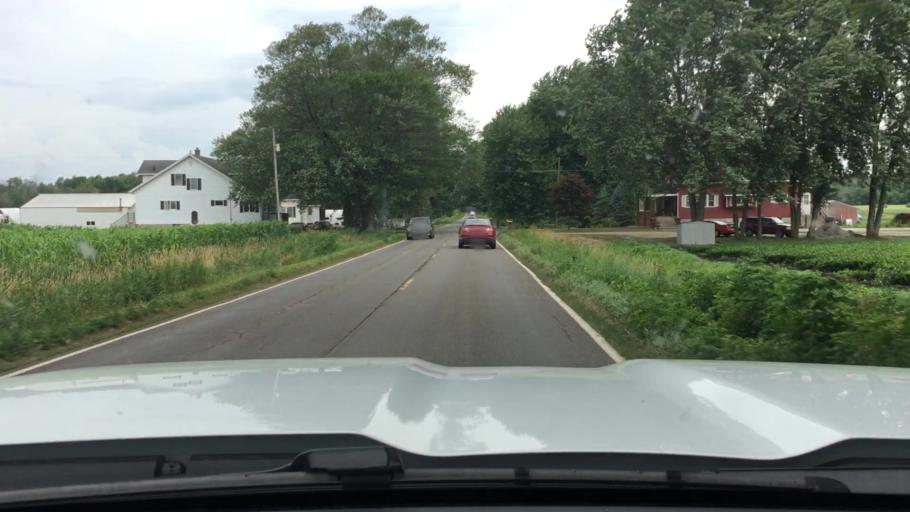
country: US
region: Michigan
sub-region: Kent County
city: Byron Center
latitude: 42.7829
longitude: -85.7289
